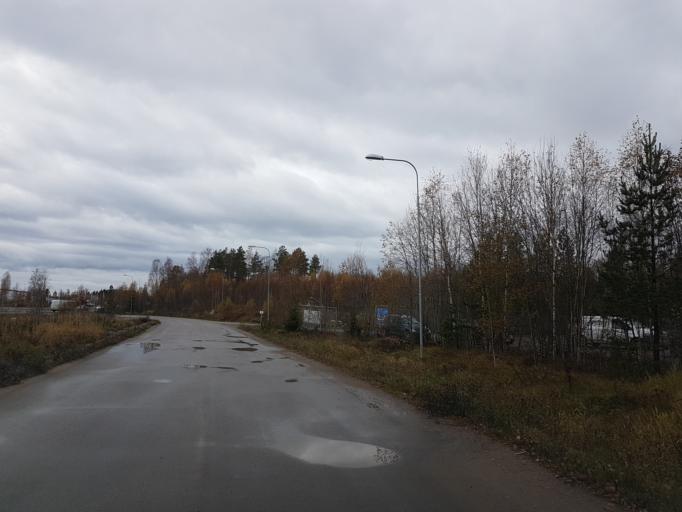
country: SE
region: Gaevleborg
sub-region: Soderhamns Kommun
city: Soderhamn
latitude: 61.2978
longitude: 17.0203
